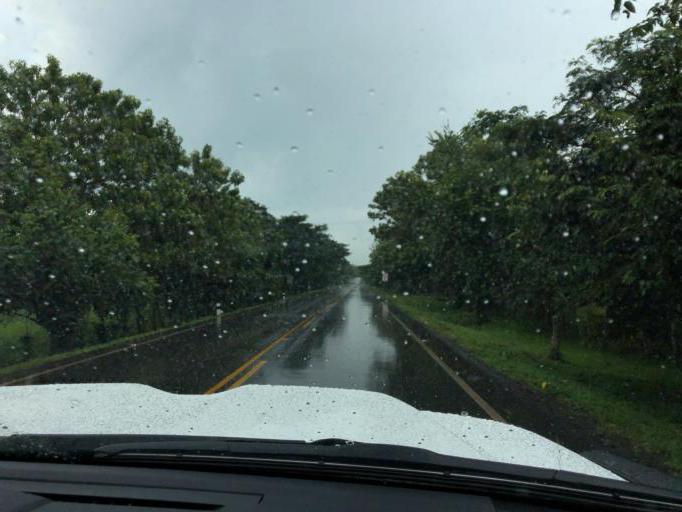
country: NI
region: Chontales
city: Villa Sandino
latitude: 12.0450
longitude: -84.9877
